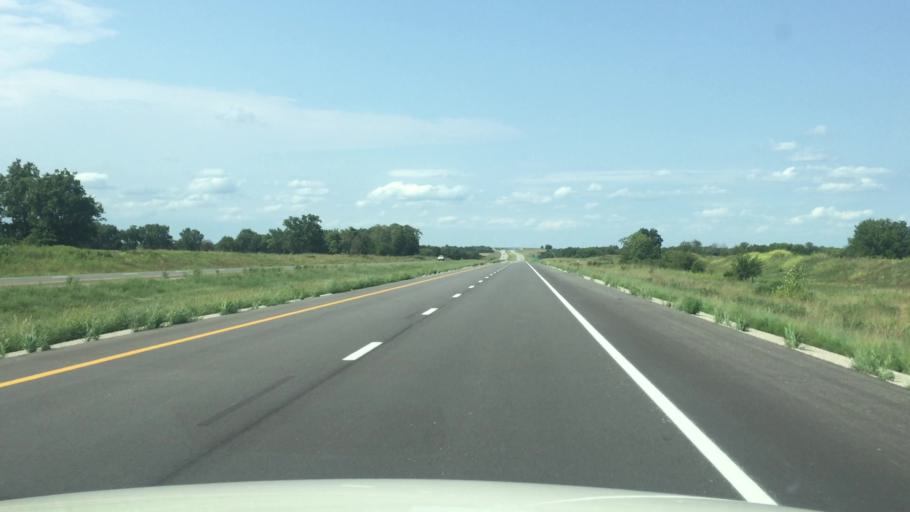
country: US
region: Kansas
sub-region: Linn County
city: La Cygne
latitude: 38.3769
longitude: -94.6874
